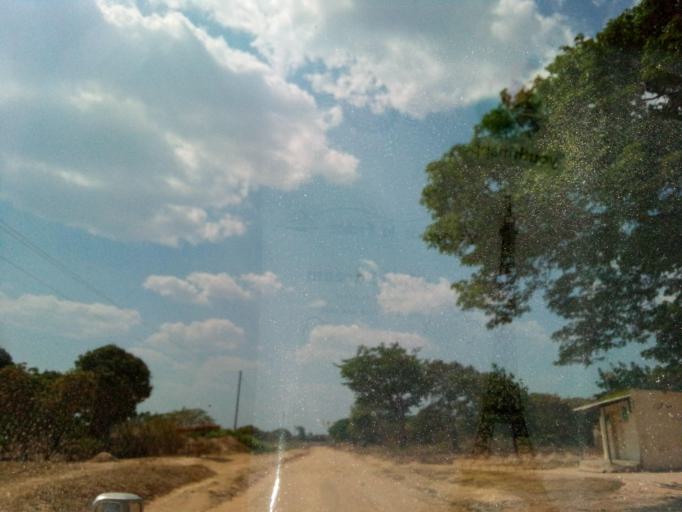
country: ZM
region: Northern
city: Mpika
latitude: -11.8403
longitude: 31.3846
